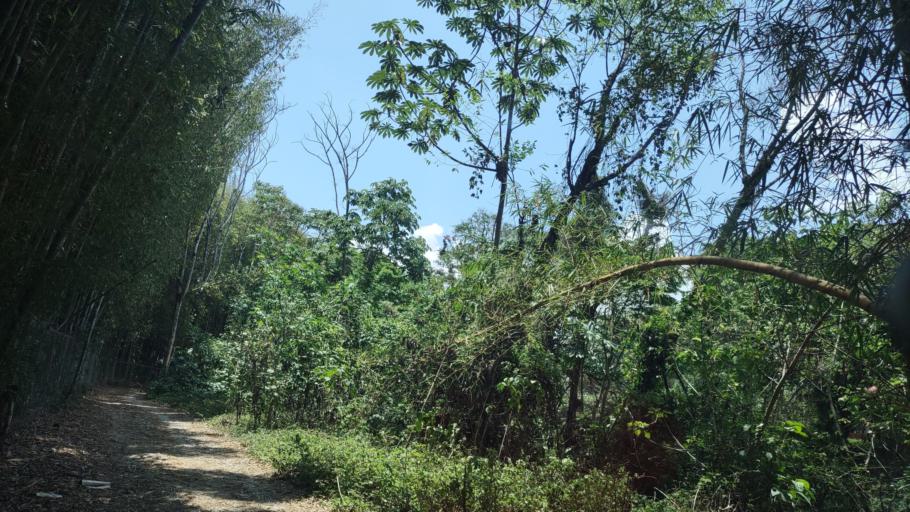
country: MX
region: Veracruz
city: Coatepec
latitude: 19.4489
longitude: -96.9503
